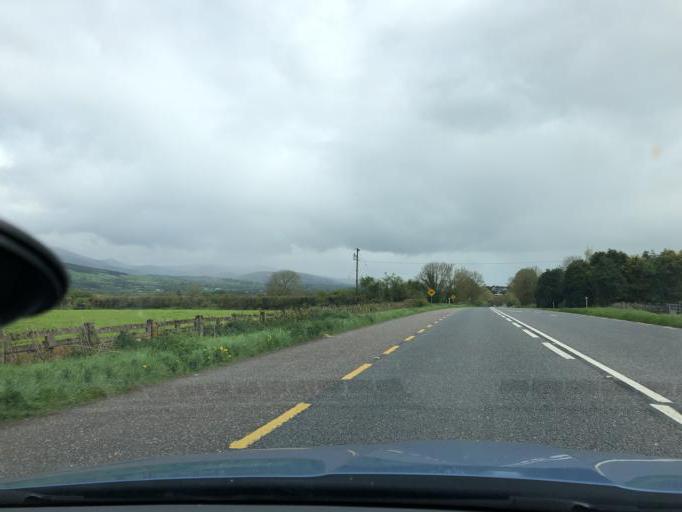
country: IE
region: Munster
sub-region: County Cork
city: Mitchelstown
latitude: 52.2823
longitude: -8.2391
